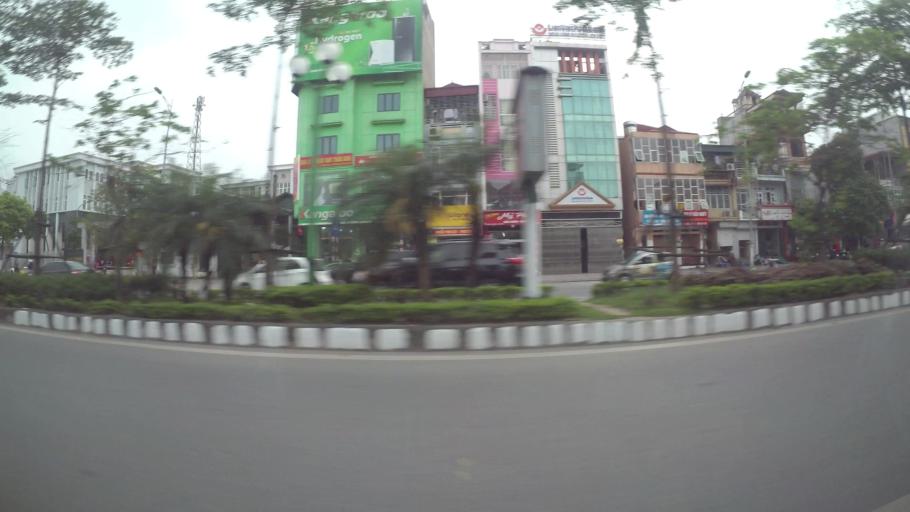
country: VN
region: Ha Noi
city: Hoan Kiem
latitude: 21.0565
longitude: 105.8895
